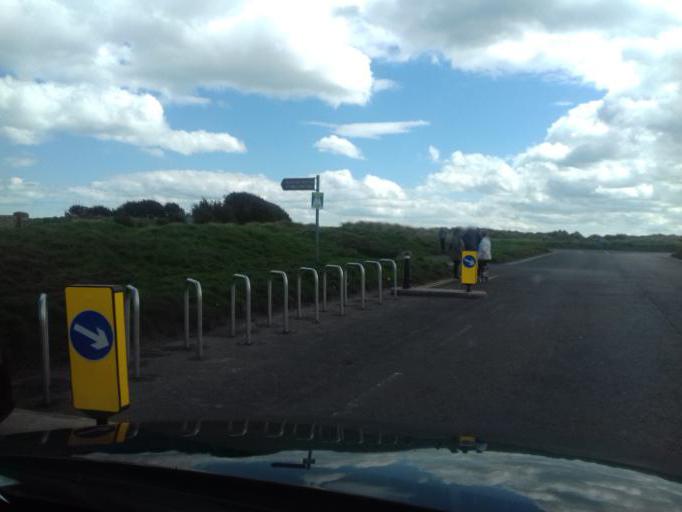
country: IE
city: Bayside
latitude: 53.3698
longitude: -6.1490
